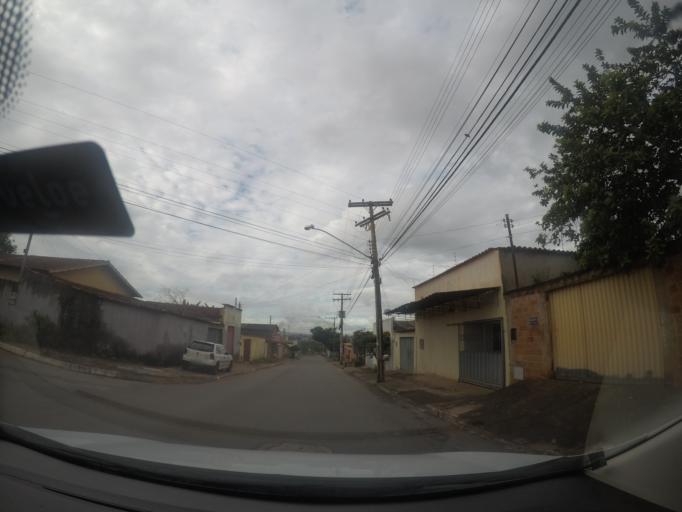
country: BR
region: Goias
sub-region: Goiania
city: Goiania
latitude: -16.6111
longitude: -49.3325
